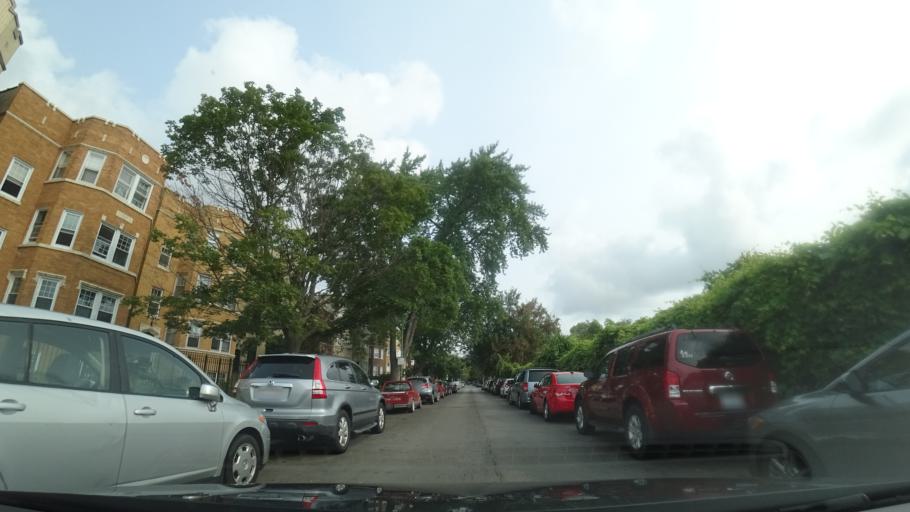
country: US
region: Illinois
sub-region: Cook County
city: Lincolnwood
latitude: 41.9931
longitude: -87.6873
